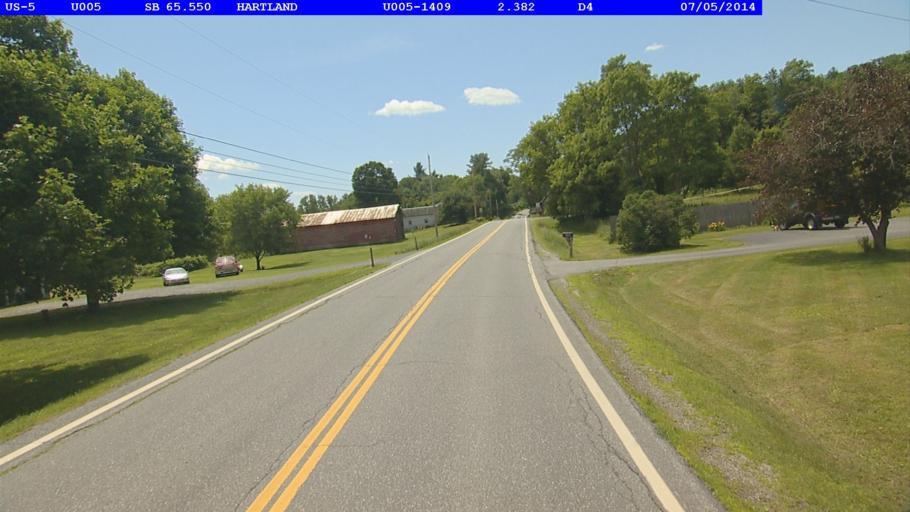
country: US
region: Vermont
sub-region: Windsor County
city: Windsor
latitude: 43.5463
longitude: -72.3871
